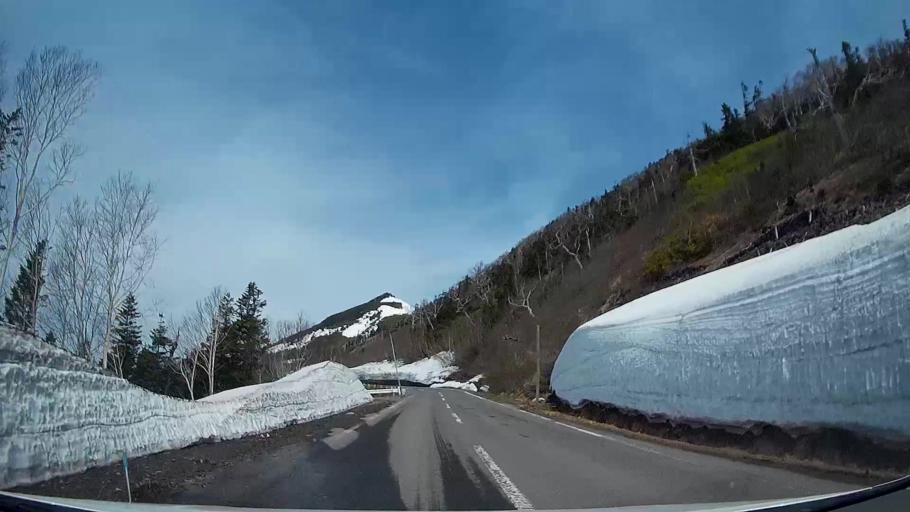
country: JP
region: Iwate
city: Shizukuishi
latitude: 39.9453
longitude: 140.9045
